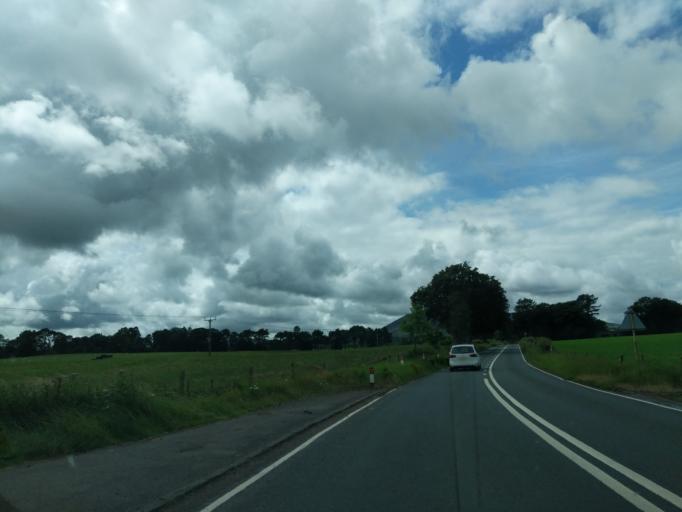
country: GB
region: Scotland
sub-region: South Lanarkshire
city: Biggar
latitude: 55.6089
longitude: -3.5604
